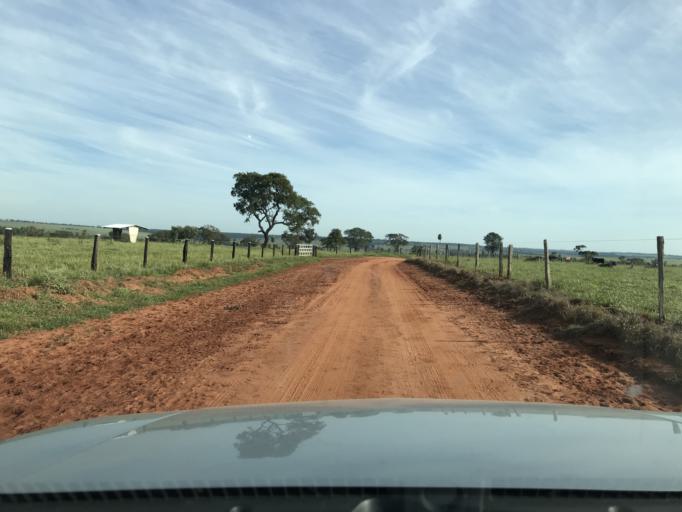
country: BR
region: Mato Grosso do Sul
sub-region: Iguatemi
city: Iguatemi
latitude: -23.6554
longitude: -54.5725
